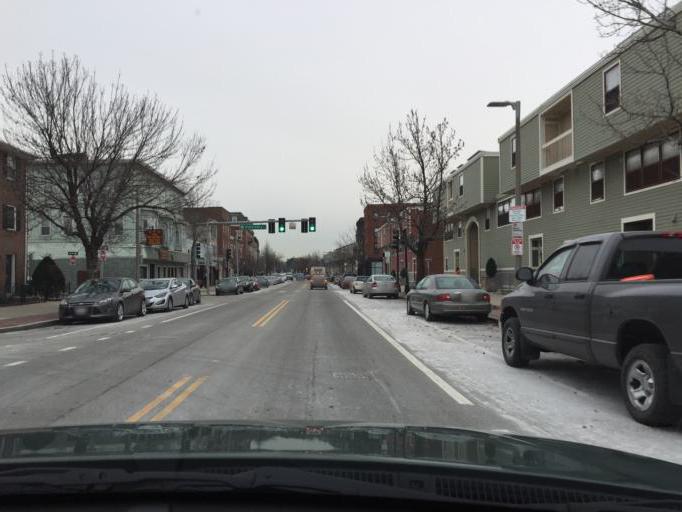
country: US
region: Massachusetts
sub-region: Suffolk County
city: Boston
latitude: 42.3781
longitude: -71.0677
